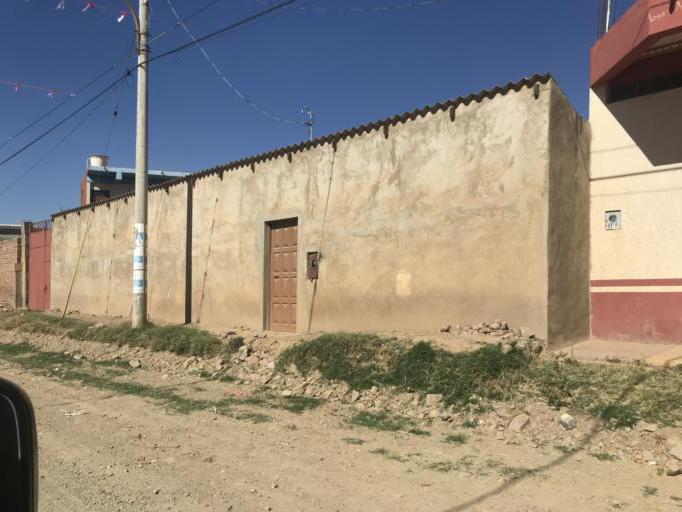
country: BO
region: Cochabamba
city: Cliza
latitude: -17.5887
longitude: -65.9253
